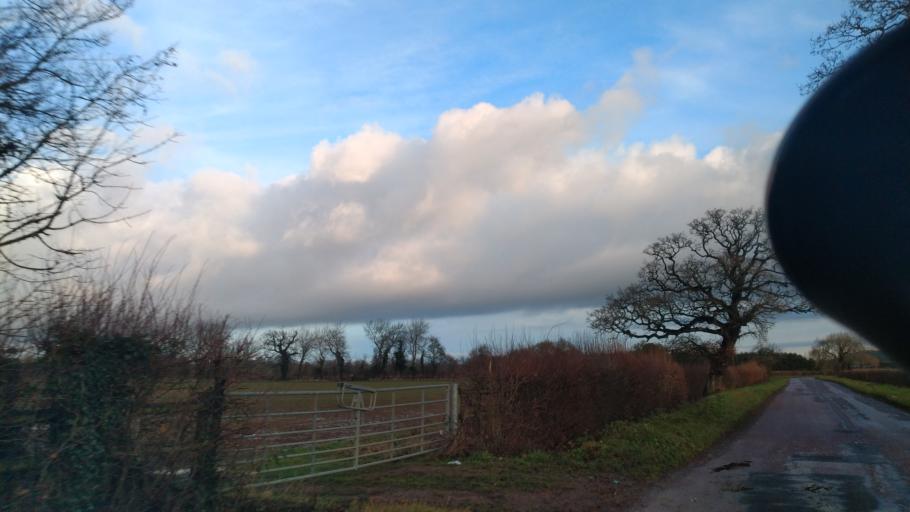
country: GB
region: England
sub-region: Wiltshire
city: Chippenham
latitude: 51.4652
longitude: -2.1555
